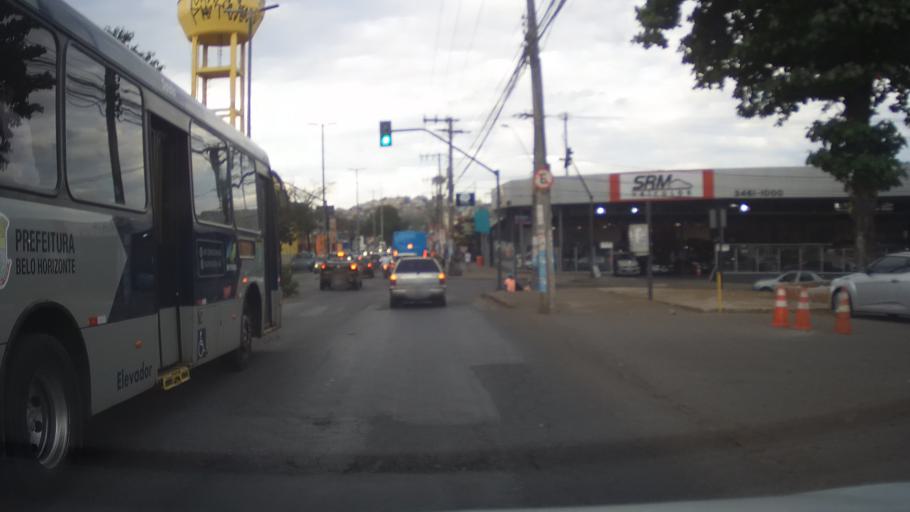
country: BR
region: Minas Gerais
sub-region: Contagem
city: Contagem
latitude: -19.9614
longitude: -44.0164
